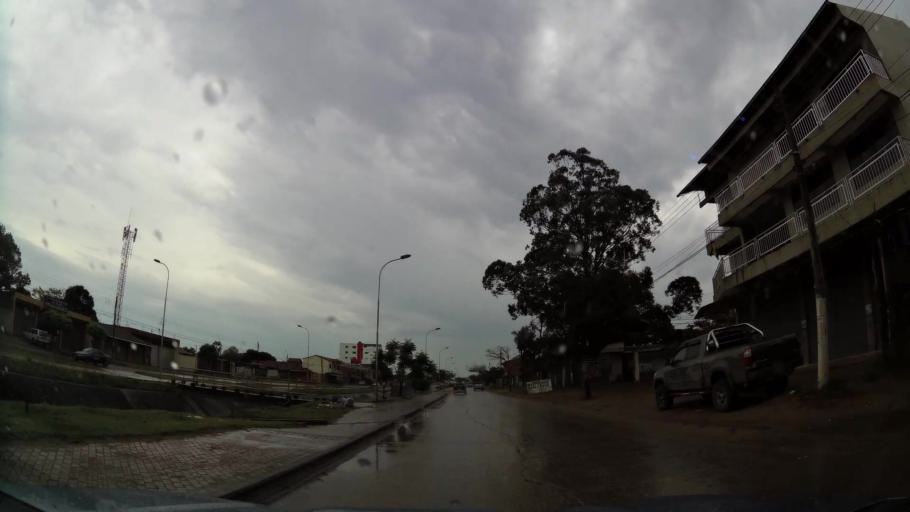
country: BO
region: Santa Cruz
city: Santa Cruz de la Sierra
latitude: -17.8118
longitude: -63.1311
